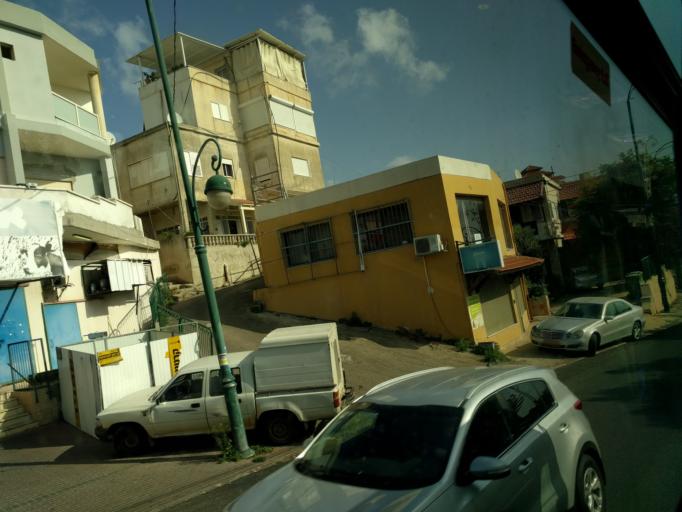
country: IL
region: Haifa
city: Daliyat el Karmil
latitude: 32.7187
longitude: 35.0649
